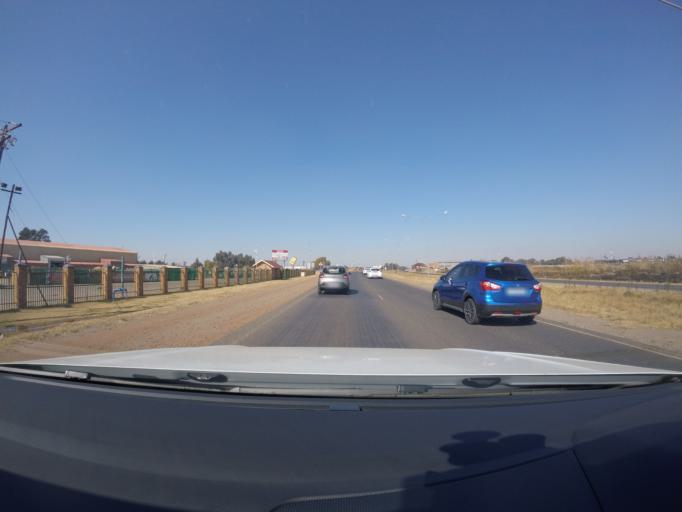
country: ZA
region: Gauteng
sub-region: Ekurhuleni Metropolitan Municipality
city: Benoni
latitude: -26.1228
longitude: 28.2850
